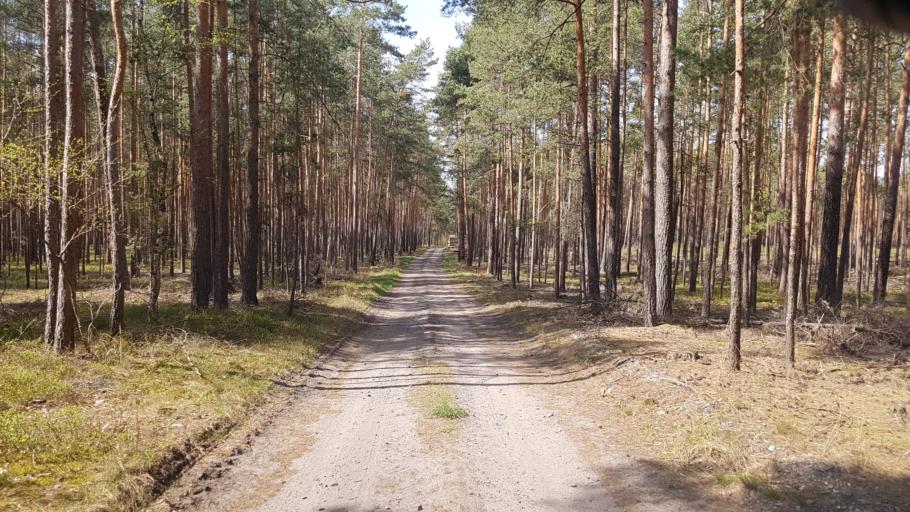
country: DE
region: Brandenburg
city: Ruckersdorf
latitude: 51.5520
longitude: 13.6347
